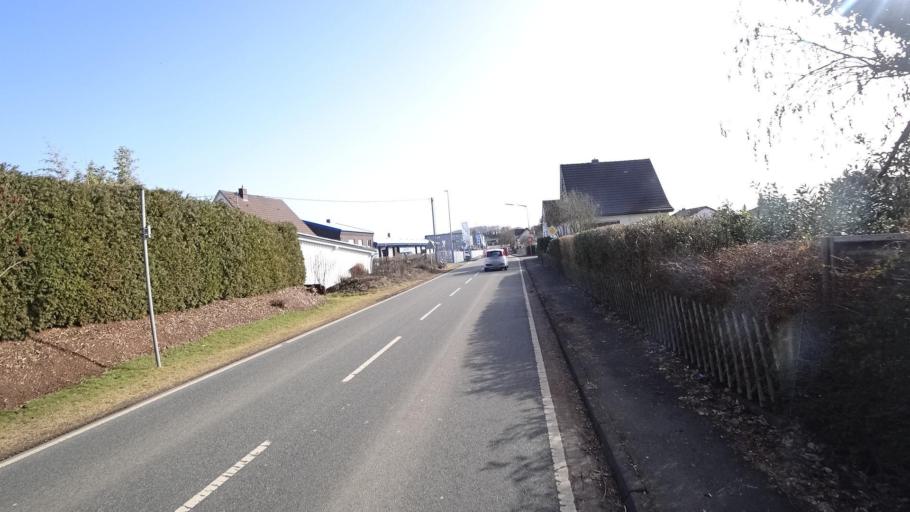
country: DE
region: Rheinland-Pfalz
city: Roth
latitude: 50.7677
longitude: 7.7011
